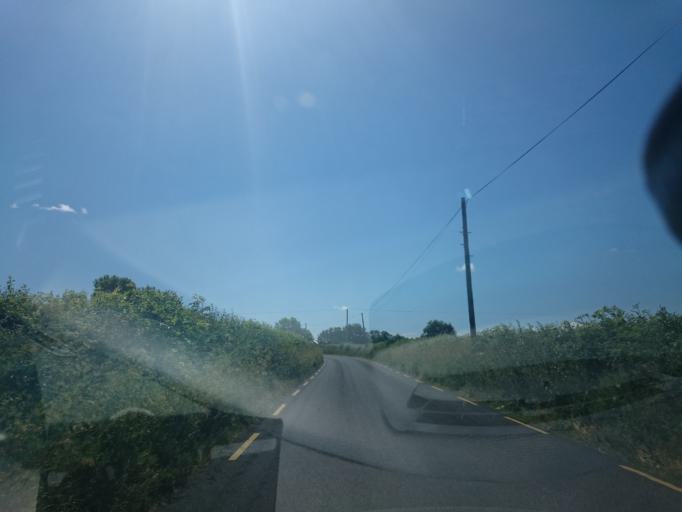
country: IE
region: Leinster
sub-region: Kilkenny
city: Graiguenamanagh
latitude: 52.5968
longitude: -6.9893
